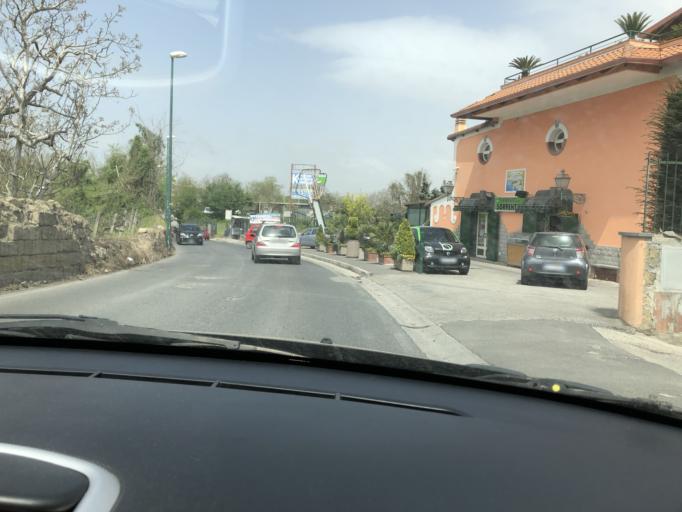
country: IT
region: Campania
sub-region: Provincia di Napoli
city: Torre Caracciolo
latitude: 40.8750
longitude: 14.1867
